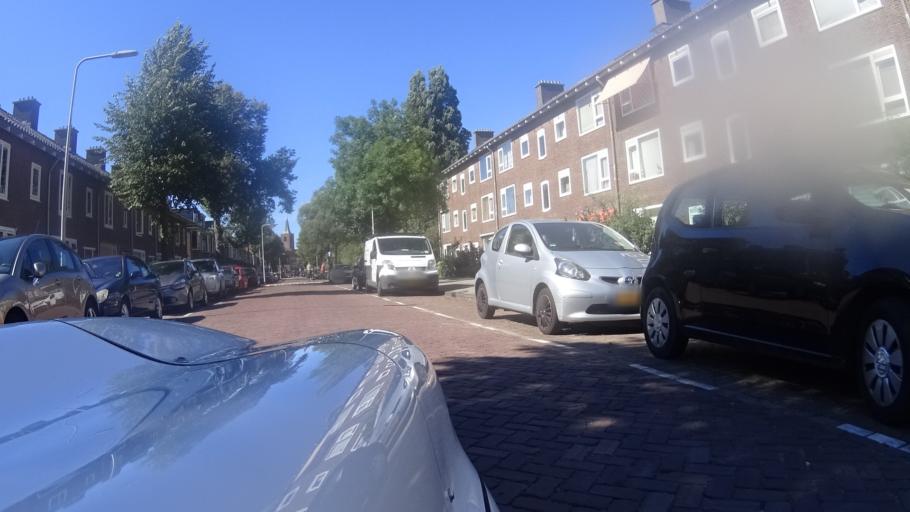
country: NL
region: South Holland
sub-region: Gemeente Leiden
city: Leiden
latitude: 52.1456
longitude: 4.4985
